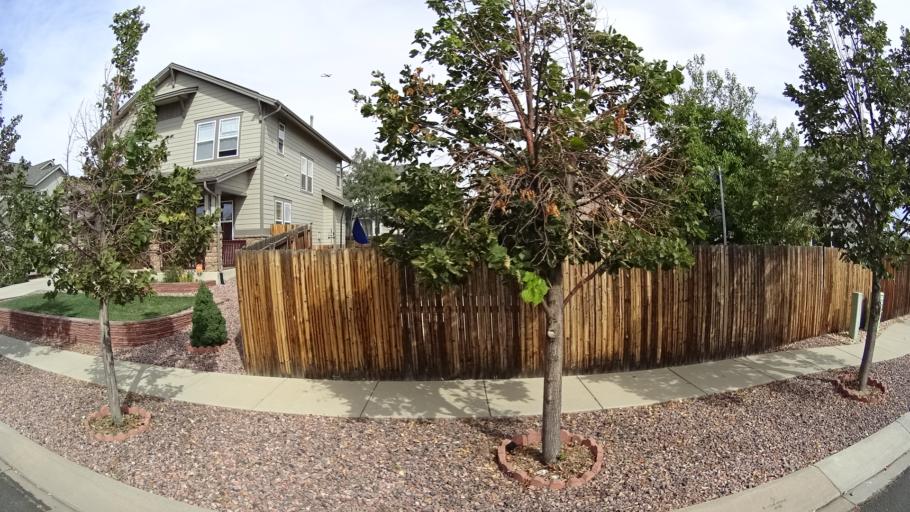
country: US
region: Colorado
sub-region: El Paso County
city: Cimarron Hills
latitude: 38.9104
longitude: -104.6965
